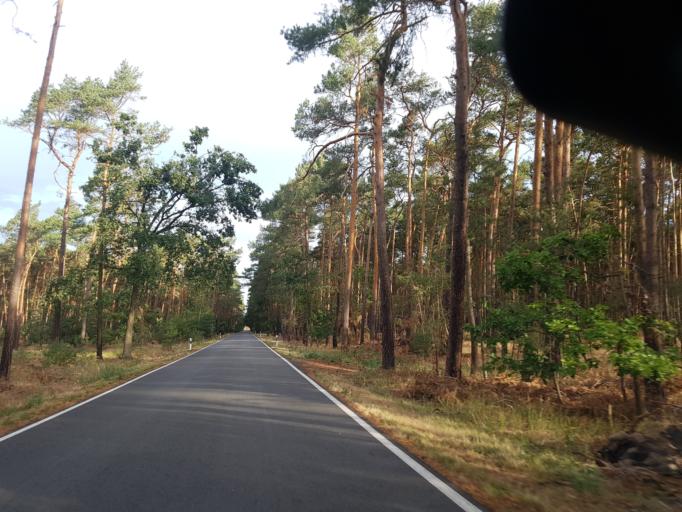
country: DE
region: Saxony-Anhalt
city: Holzdorf
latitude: 51.7958
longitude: 13.0996
